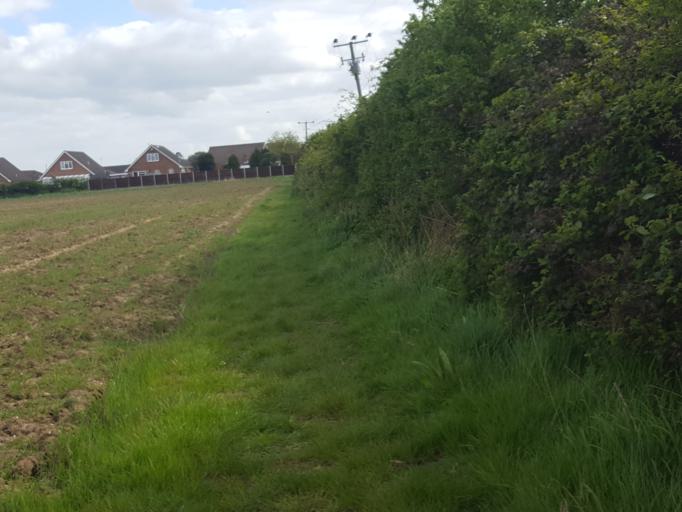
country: GB
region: England
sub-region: Essex
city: Frinton-on-Sea
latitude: 51.8364
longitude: 1.2076
